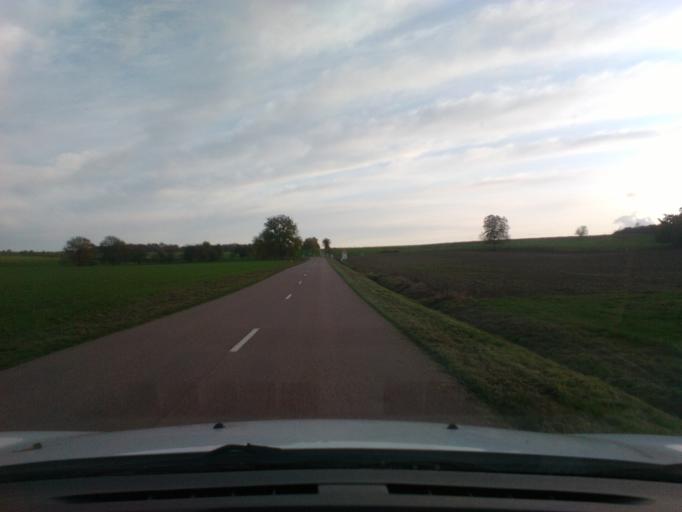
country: FR
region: Lorraine
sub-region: Departement des Vosges
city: Mirecourt
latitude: 48.2273
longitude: 6.1493
